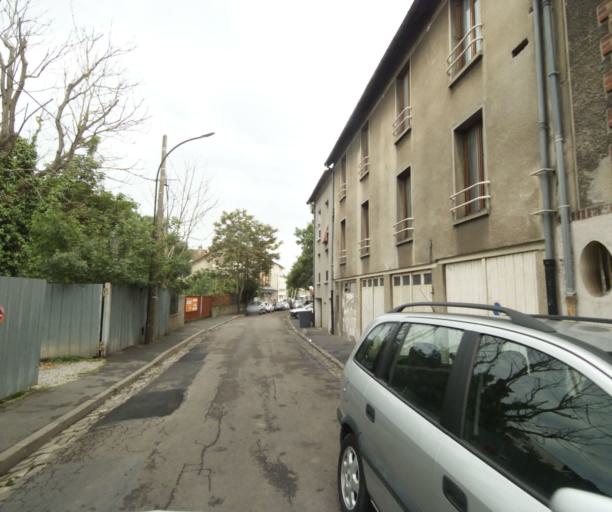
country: FR
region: Ile-de-France
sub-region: Departement du Val-d'Oise
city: Argenteuil
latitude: 48.9538
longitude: 2.2433
